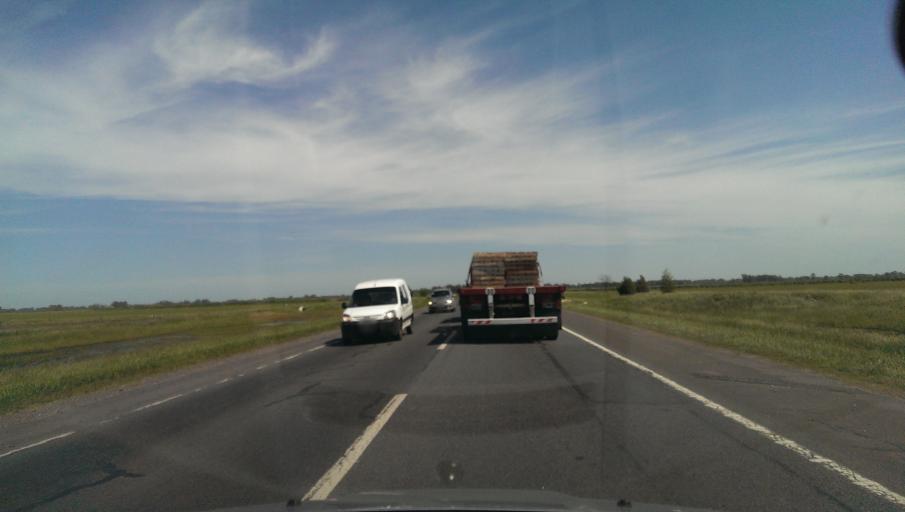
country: AR
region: Buenos Aires
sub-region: Partido de Las Flores
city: Las Flores
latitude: -35.9776
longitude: -59.0379
